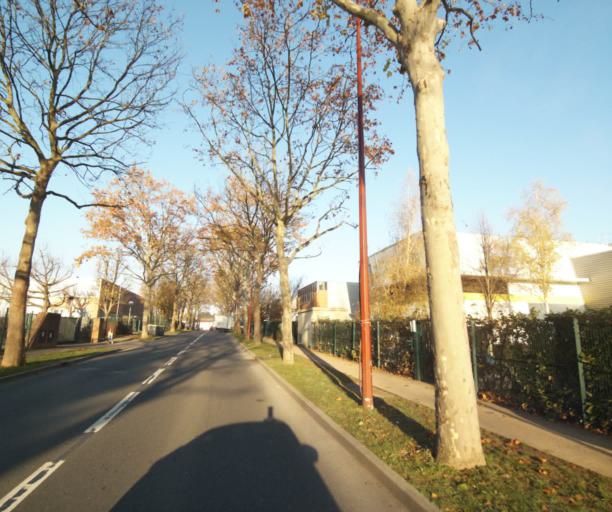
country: FR
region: Ile-de-France
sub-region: Departement du Val-d'Oise
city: Gonesse
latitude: 48.9908
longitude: 2.4345
